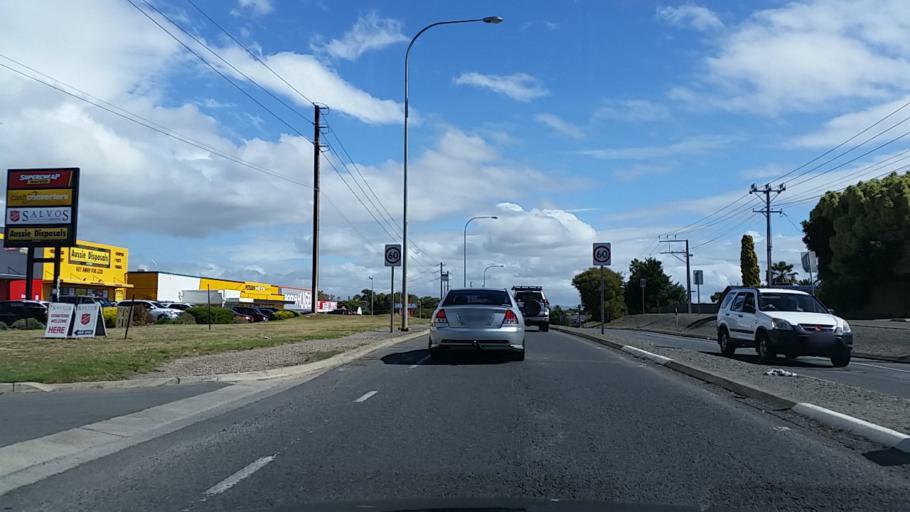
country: AU
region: South Australia
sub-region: Adelaide
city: Port Noarlunga
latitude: -35.1396
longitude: 138.4863
